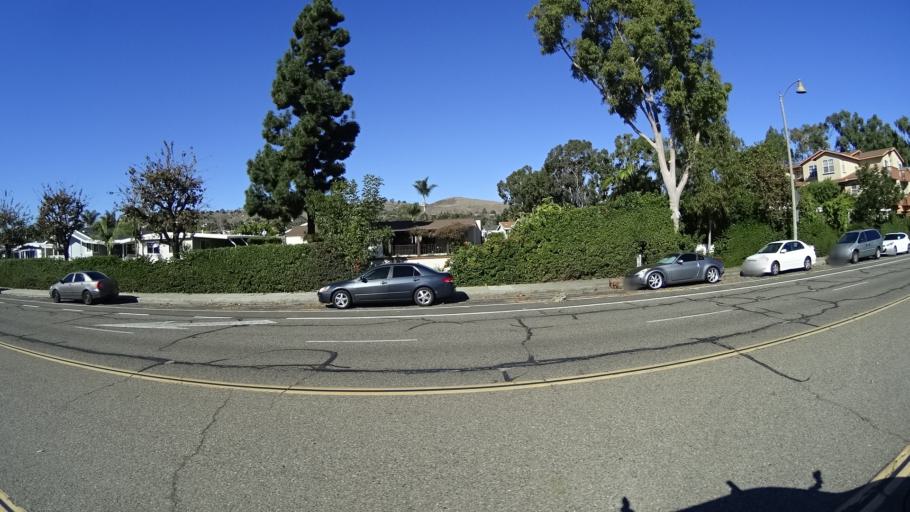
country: US
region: California
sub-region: Orange County
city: San Juan Capistrano
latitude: 33.4926
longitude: -117.6700
